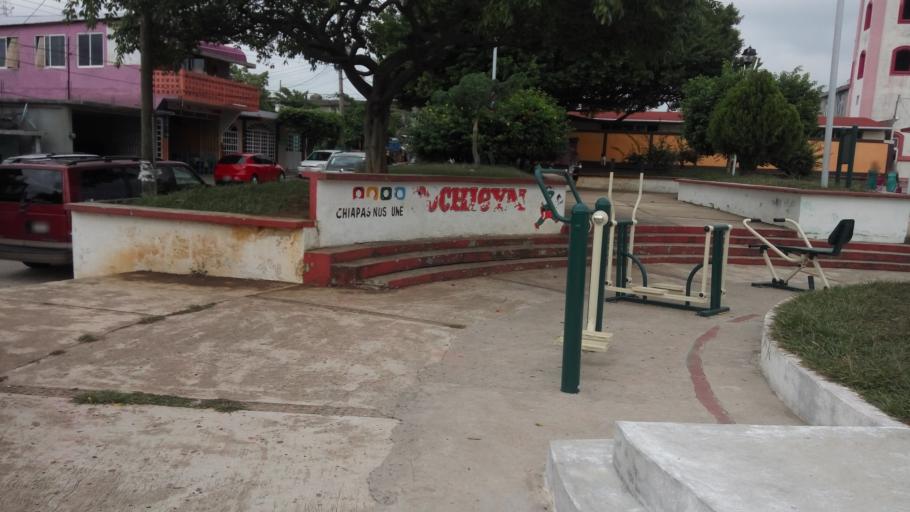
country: MX
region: Chiapas
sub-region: Reforma
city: El Carmen (El Limon)
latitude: 17.8678
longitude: -93.1466
